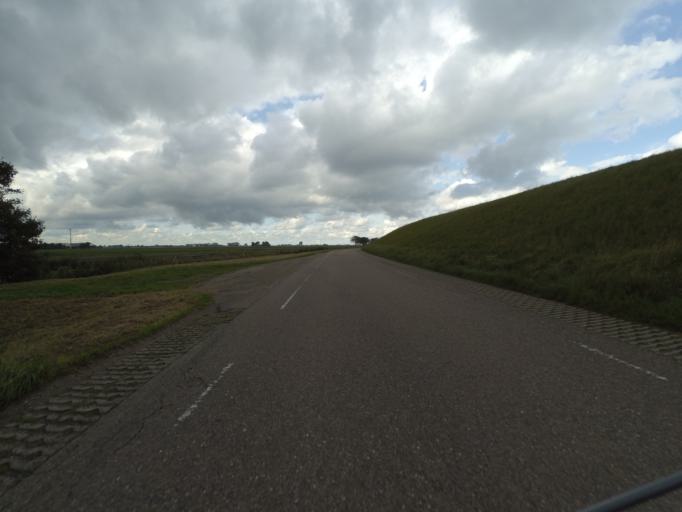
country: NL
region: North Holland
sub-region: Gemeente Schagen
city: Schagen
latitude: 52.8766
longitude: 4.8922
